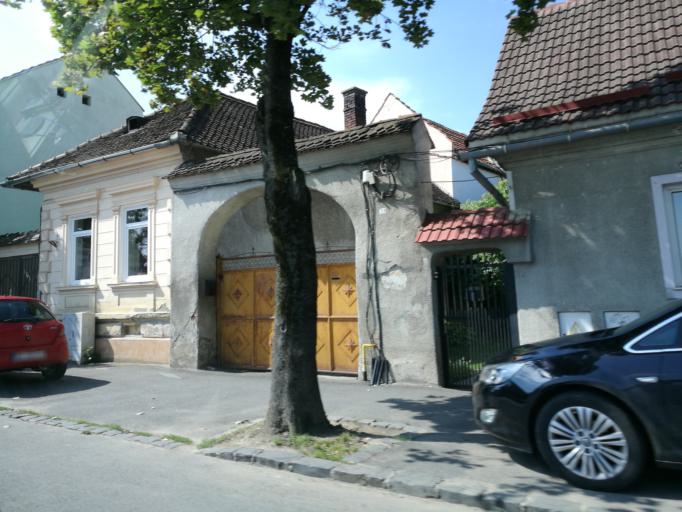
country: RO
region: Brasov
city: Brasov
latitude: 45.6573
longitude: 25.5885
